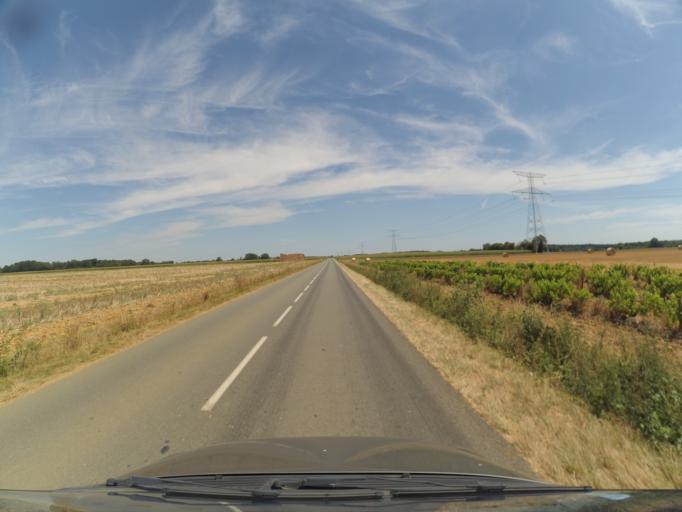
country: FR
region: Poitou-Charentes
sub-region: Departement de la Vienne
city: Saint-Maurice-la-Clouere
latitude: 46.3974
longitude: 0.3661
